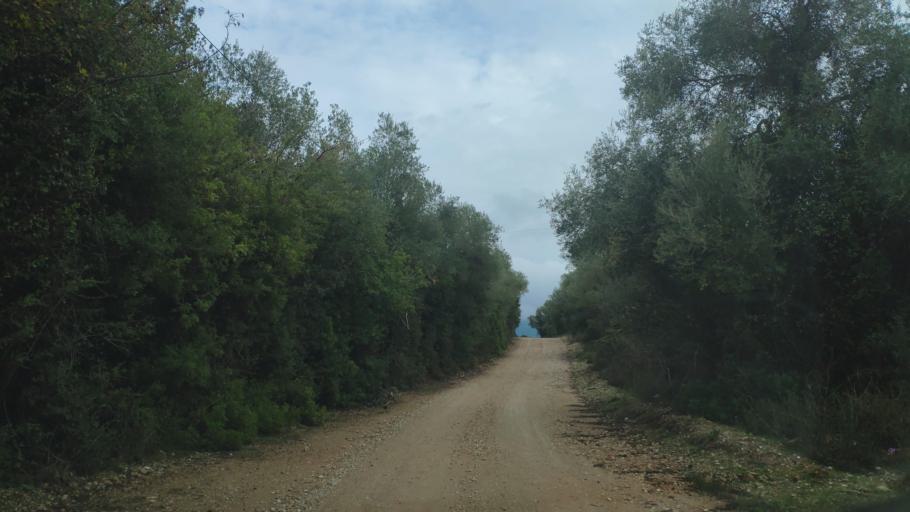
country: GR
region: West Greece
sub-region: Nomos Aitolias kai Akarnanias
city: Vonitsa
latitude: 38.9250
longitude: 20.8620
